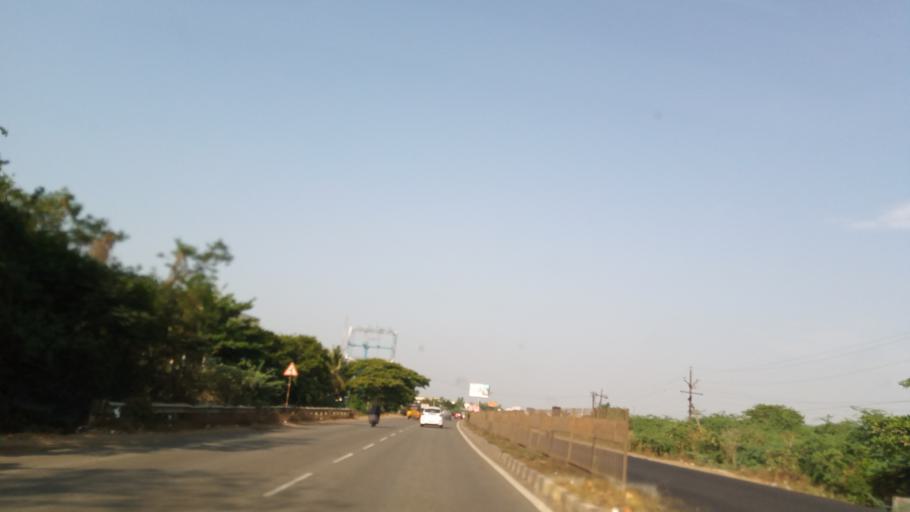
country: IN
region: Tamil Nadu
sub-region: Kancheepuram
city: Poonamalle
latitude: 13.0429
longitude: 80.0622
